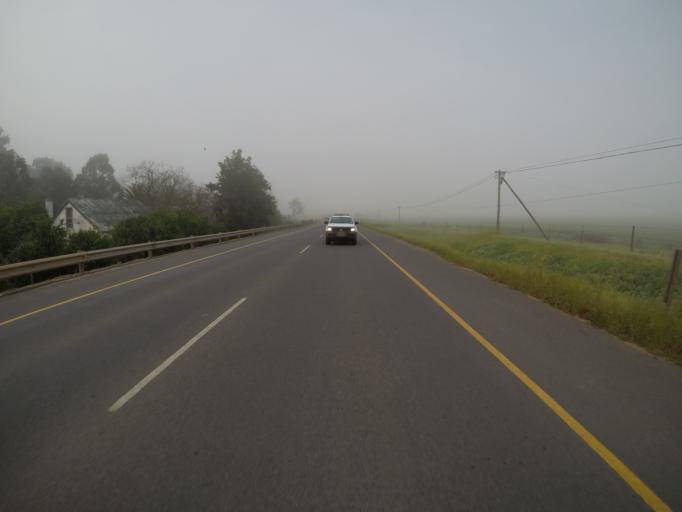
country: ZA
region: Western Cape
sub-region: City of Cape Town
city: Kraaifontein
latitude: -33.7741
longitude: 18.7089
